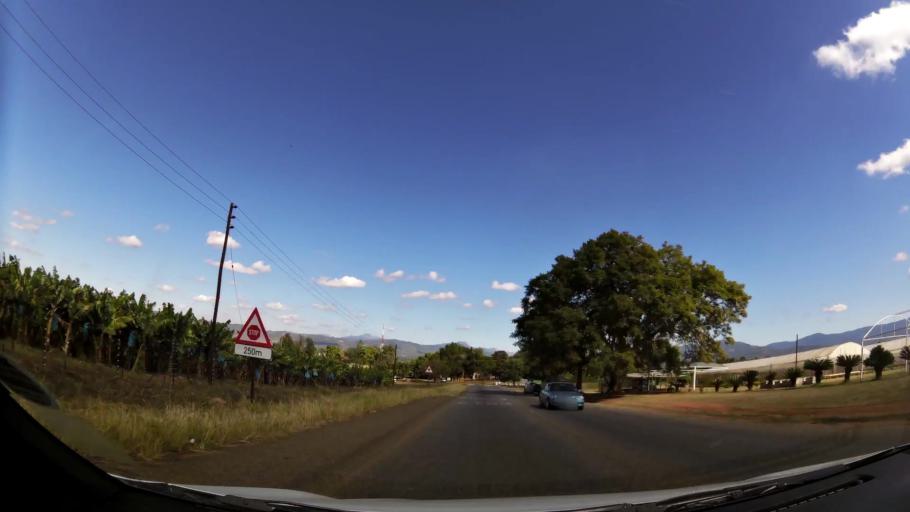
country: ZA
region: Limpopo
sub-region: Mopani District Municipality
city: Tzaneen
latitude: -23.8118
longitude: 30.1738
